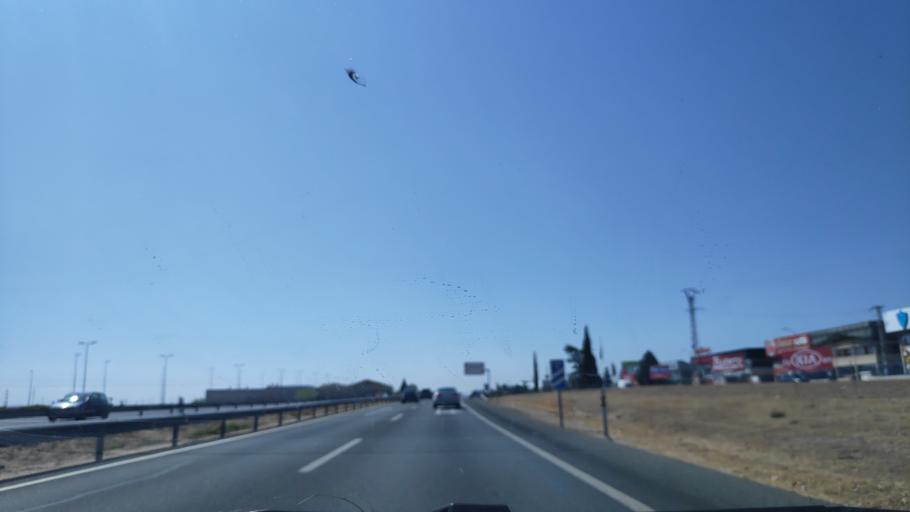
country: ES
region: Madrid
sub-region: Provincia de Madrid
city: Casarrubuelos
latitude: 40.1542
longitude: -3.8216
